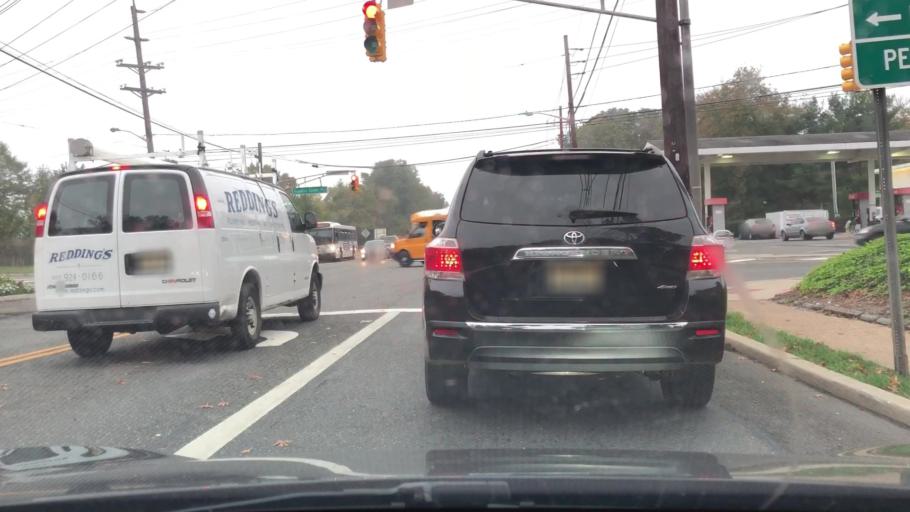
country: US
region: New Jersey
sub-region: Mercer County
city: Lawrenceville
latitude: 40.2903
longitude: -74.7339
